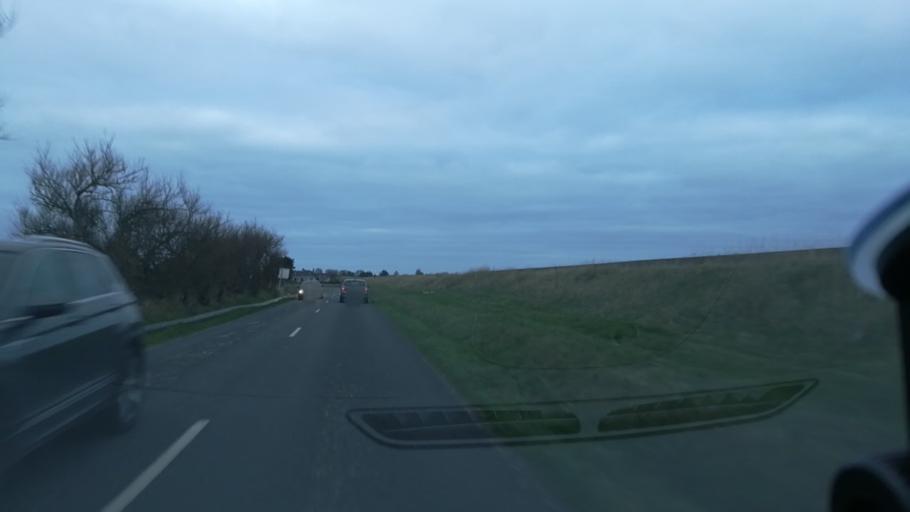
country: FR
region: Lower Normandy
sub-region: Departement de la Manche
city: Reville
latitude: 49.6033
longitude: -1.2598
